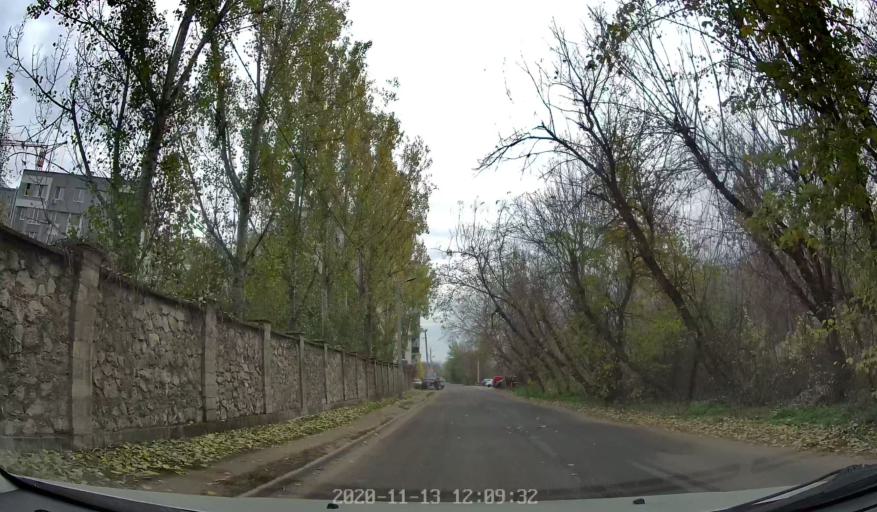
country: MD
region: Chisinau
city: Chisinau
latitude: 46.9588
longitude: 28.8363
